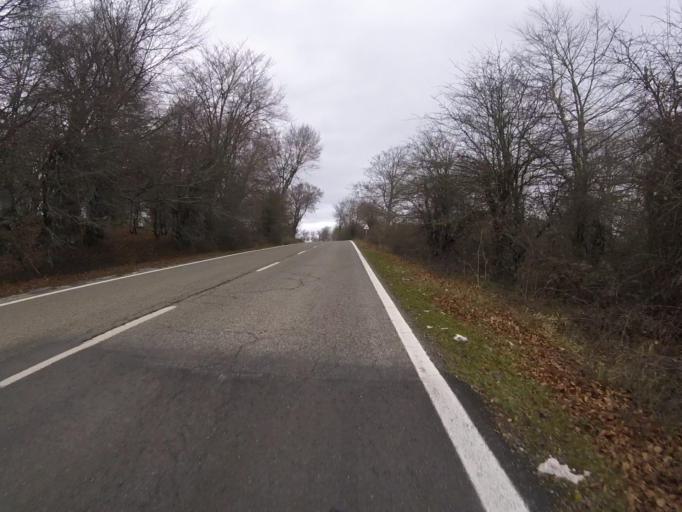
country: ES
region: Navarre
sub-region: Provincia de Navarra
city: Eulate
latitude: 42.7969
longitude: -2.1441
